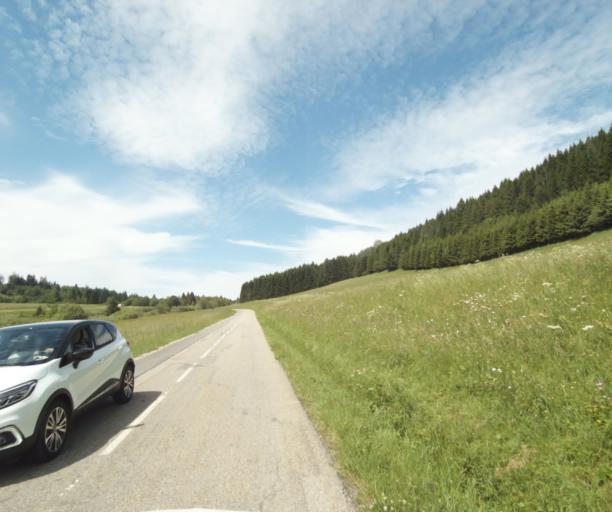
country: FR
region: Rhone-Alpes
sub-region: Departement de la Haute-Savoie
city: Perrignier
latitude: 46.2714
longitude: 6.4673
